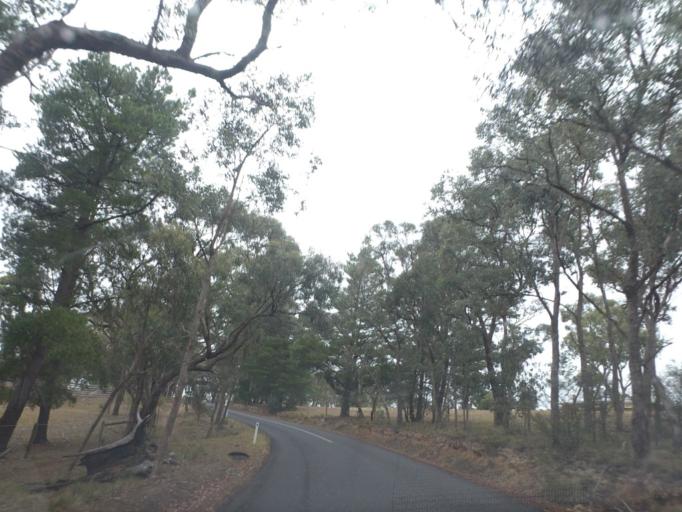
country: AU
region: Victoria
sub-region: Nillumbik
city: Saint Andrews
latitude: -37.6276
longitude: 145.2719
